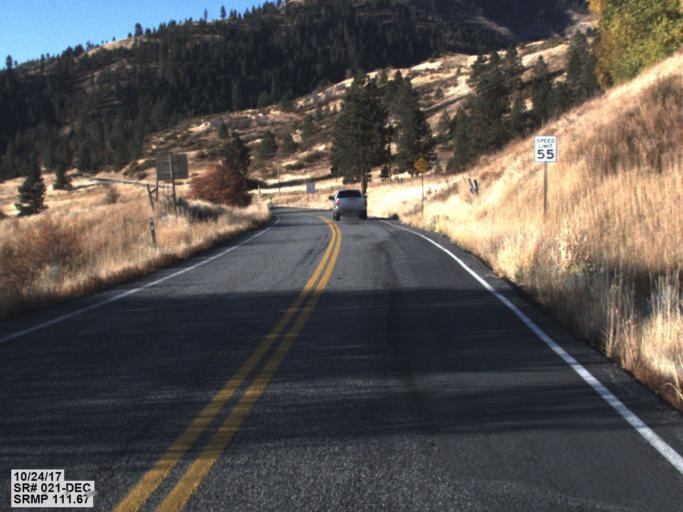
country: US
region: Washington
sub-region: Okanogan County
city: Coulee Dam
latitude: 48.0129
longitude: -118.6822
